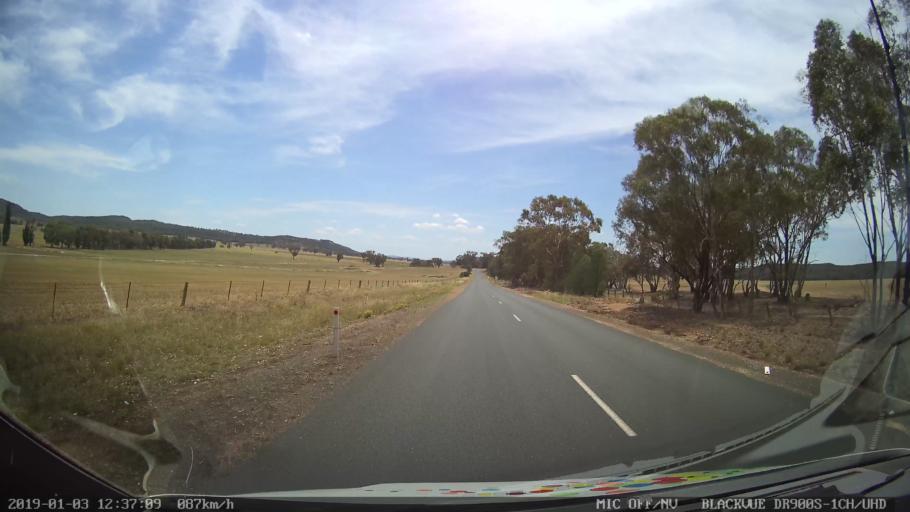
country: AU
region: New South Wales
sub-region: Weddin
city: Grenfell
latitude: -33.8459
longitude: 148.1815
